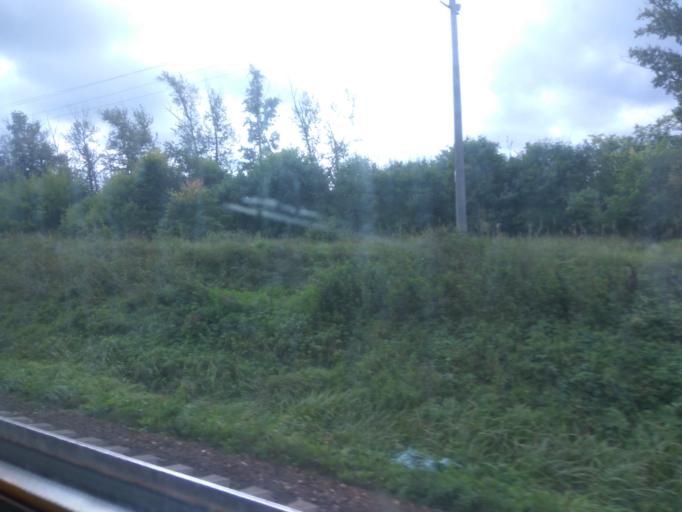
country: RU
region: Moskovskaya
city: Beloozerskiy
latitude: 55.4768
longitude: 38.4167
